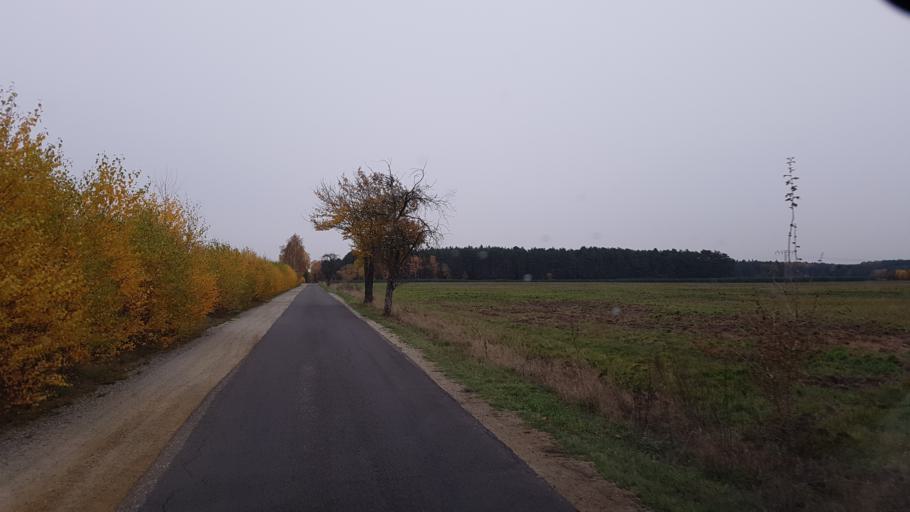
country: DE
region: Brandenburg
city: Crinitz
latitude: 51.7220
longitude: 13.7734
